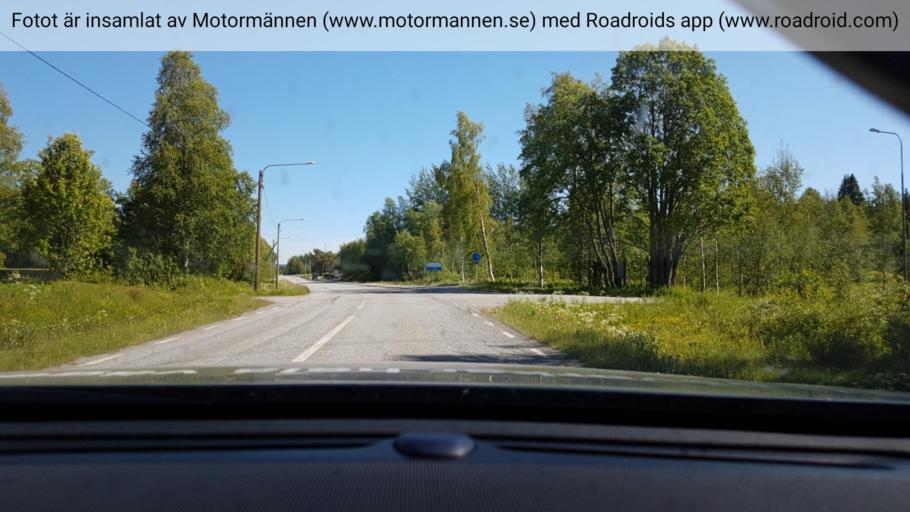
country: SE
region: Vaesterbotten
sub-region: Vilhelmina Kommun
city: Sjoberg
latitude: 64.6401
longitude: 16.3595
